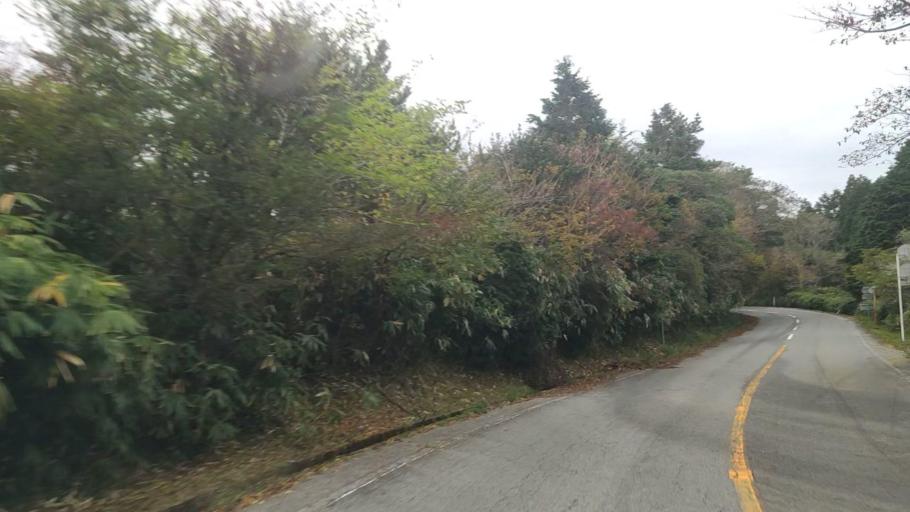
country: JP
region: Shizuoka
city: Heda
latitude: 34.9294
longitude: 138.8391
